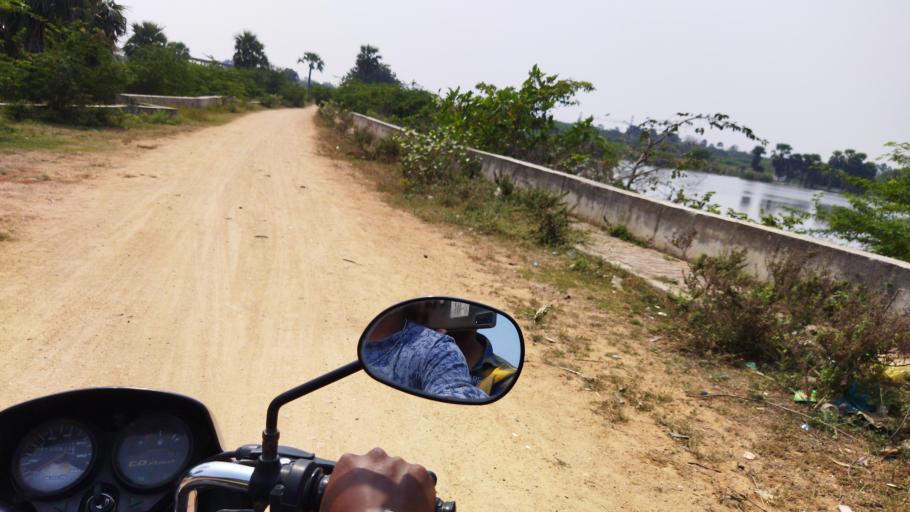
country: IN
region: Telangana
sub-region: Nalgonda
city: Nalgonda
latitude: 17.1626
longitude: 79.4191
